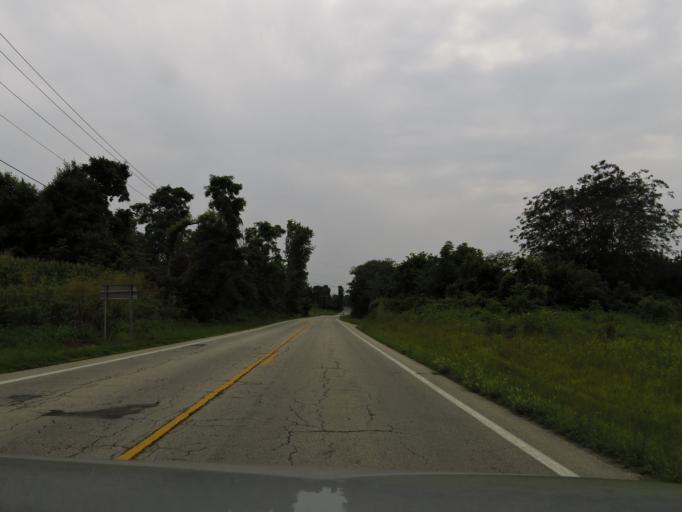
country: US
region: Ohio
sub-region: Clinton County
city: Blanchester
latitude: 39.2557
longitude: -83.9036
